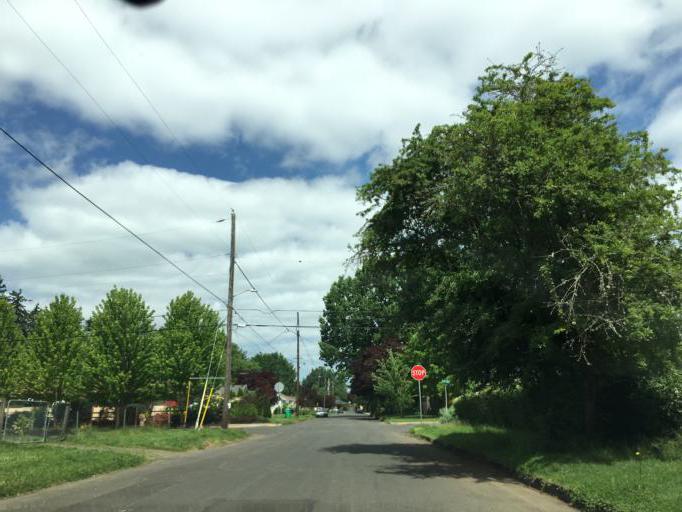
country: US
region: Oregon
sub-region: Multnomah County
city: Lents
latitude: 45.4824
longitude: -122.6097
